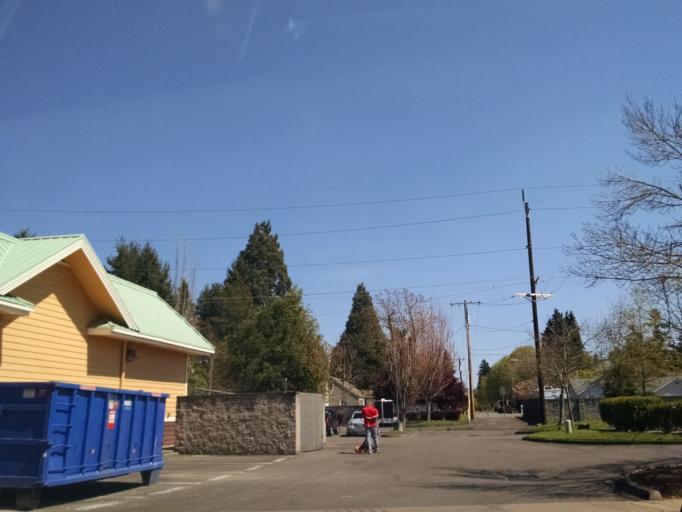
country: US
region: Oregon
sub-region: Lane County
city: Springfield
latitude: 44.0835
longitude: -123.0380
